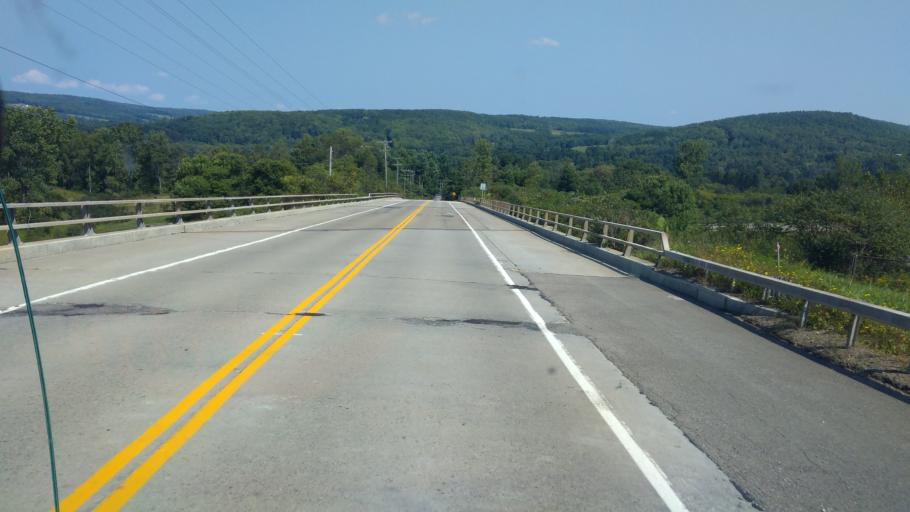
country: US
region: New York
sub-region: Allegany County
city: Belmont
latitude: 42.2982
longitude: -78.0261
